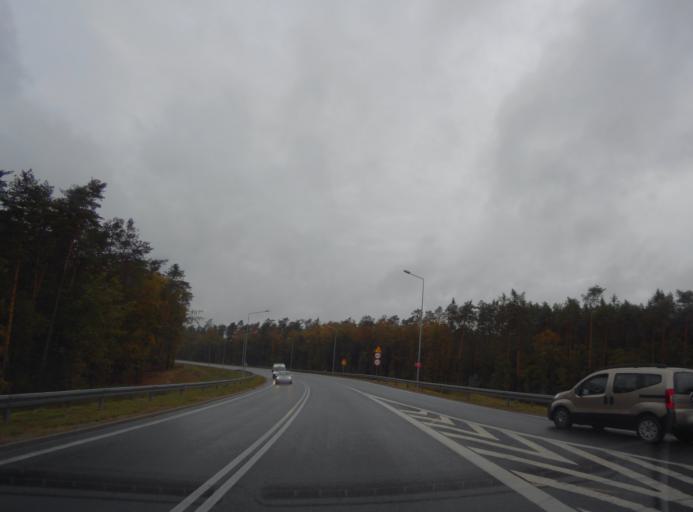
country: PL
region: Subcarpathian Voivodeship
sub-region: Powiat lezajski
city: Lezajsk
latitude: 50.2775
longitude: 22.3998
